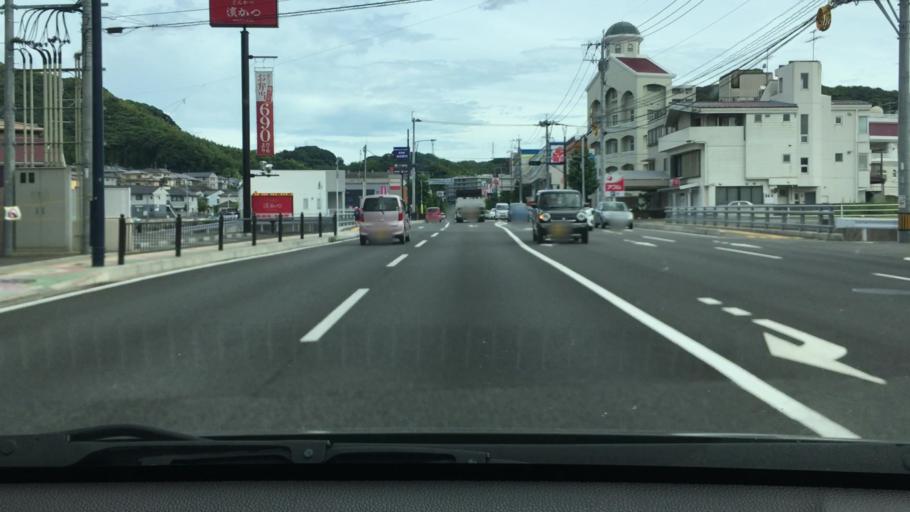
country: JP
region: Nagasaki
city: Togitsu
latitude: 32.8281
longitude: 129.8479
